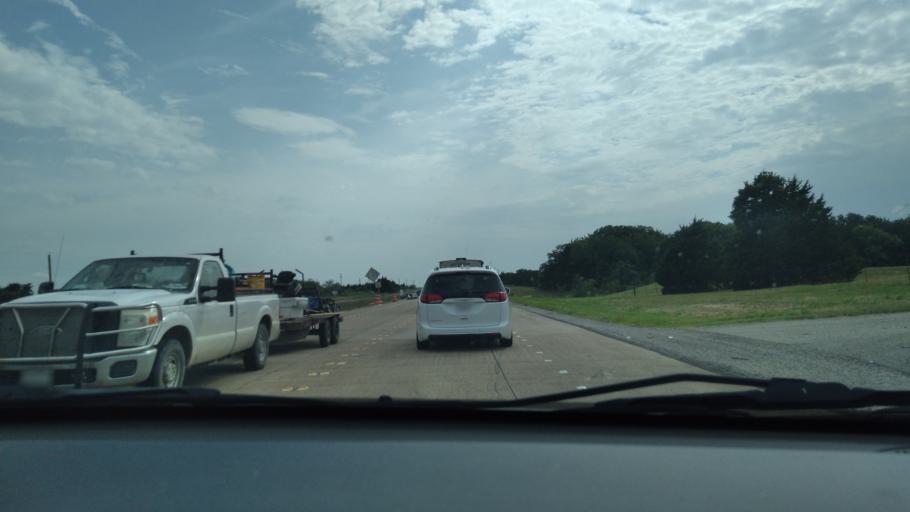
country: US
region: Texas
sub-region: Hill County
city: Hubbard
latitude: 31.8758
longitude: -96.7591
